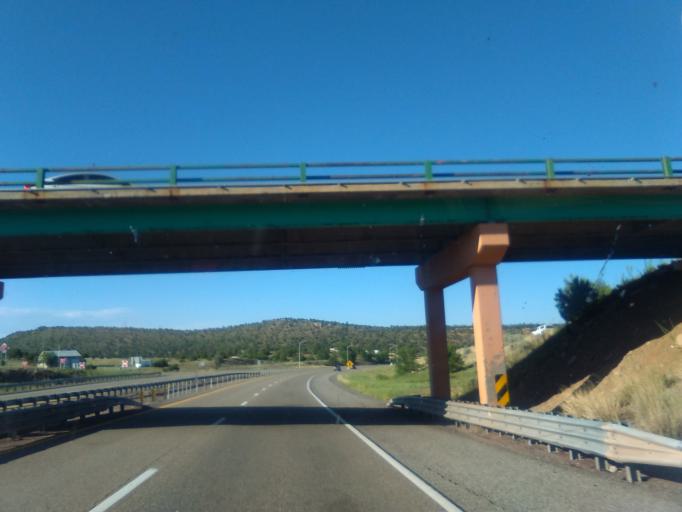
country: US
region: New Mexico
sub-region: San Miguel County
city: Las Vegas
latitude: 35.5204
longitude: -105.2499
